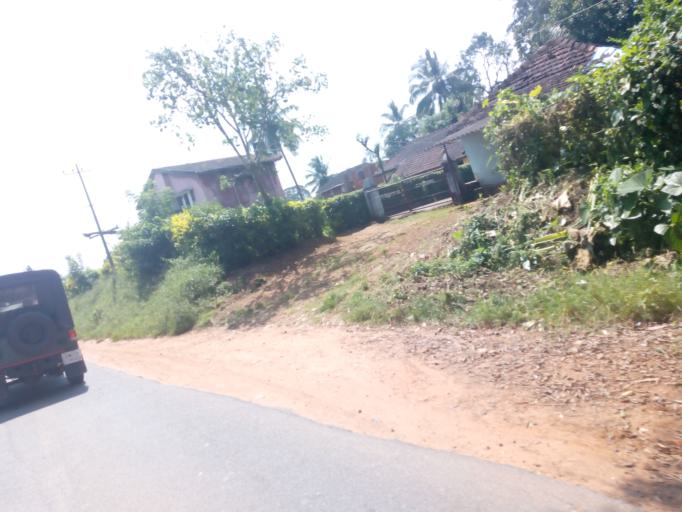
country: IN
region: Karnataka
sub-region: Kodagu
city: Ponnampet
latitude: 12.0874
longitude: 75.9401
